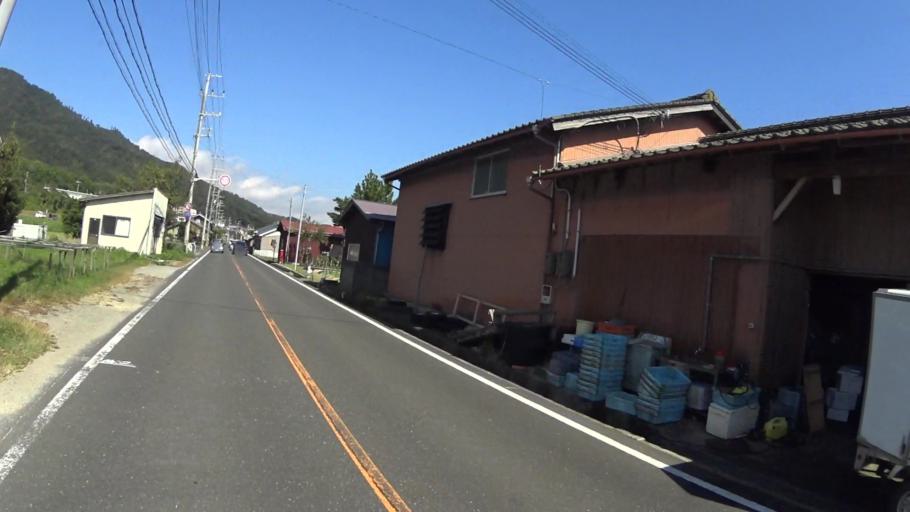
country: JP
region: Kyoto
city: Miyazu
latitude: 35.5896
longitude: 135.1936
